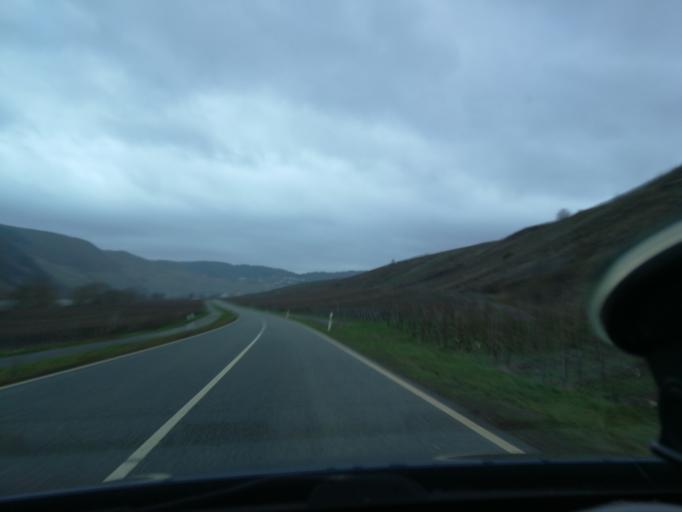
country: DE
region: Rheinland-Pfalz
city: Neumagen-Dhron
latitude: 49.8418
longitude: 6.8918
